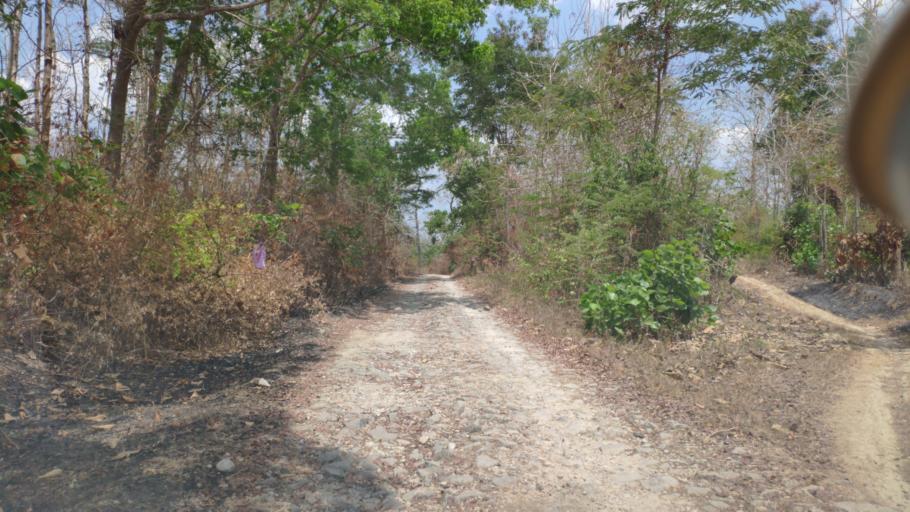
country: ID
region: Central Java
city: Suruhan
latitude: -6.9969
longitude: 111.5236
